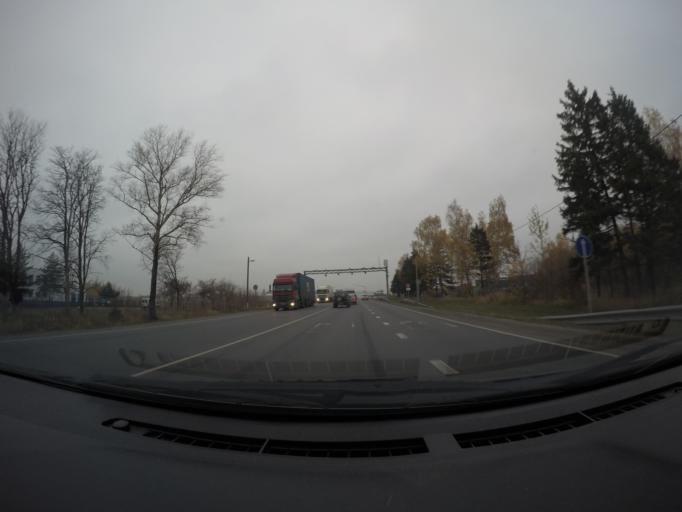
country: RU
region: Moskovskaya
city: Bronnitsy
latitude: 55.4156
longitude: 38.2504
